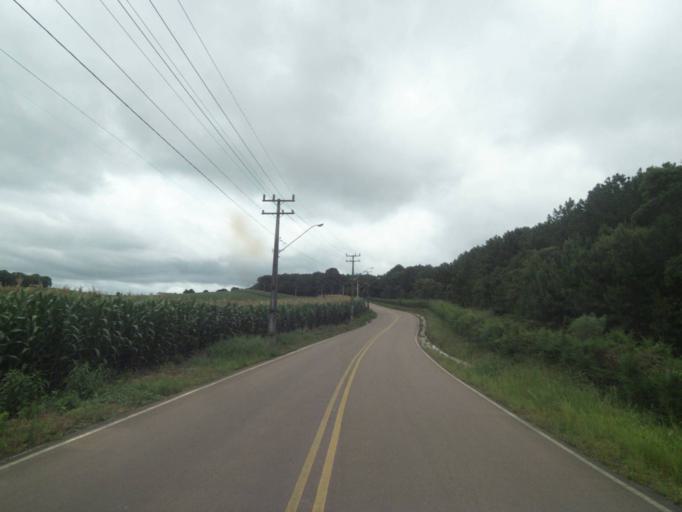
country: BR
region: Parana
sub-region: Campina Grande Do Sul
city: Campina Grande do Sul
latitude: -25.3144
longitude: -49.0298
